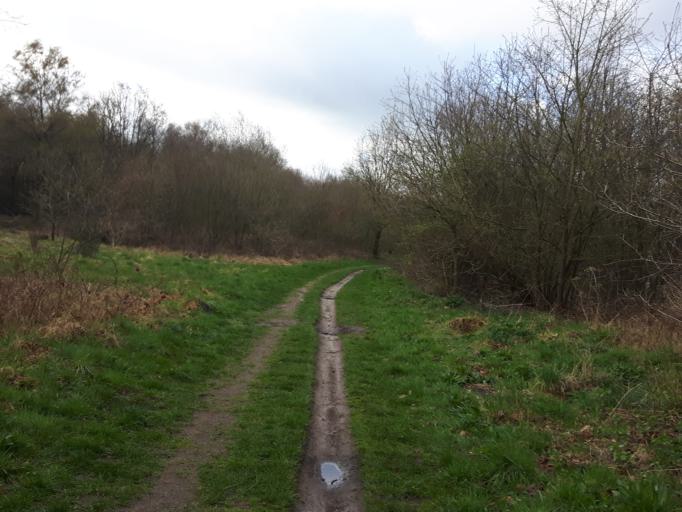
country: NL
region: Overijssel
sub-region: Gemeente Enschede
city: Enschede
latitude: 52.1760
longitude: 6.8389
